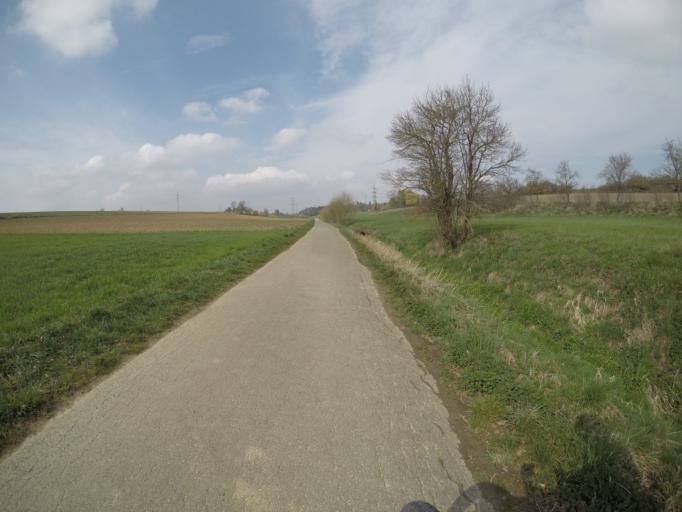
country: DE
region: Baden-Wuerttemberg
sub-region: Regierungsbezirk Stuttgart
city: Nufringen
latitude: 48.6267
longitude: 8.8802
